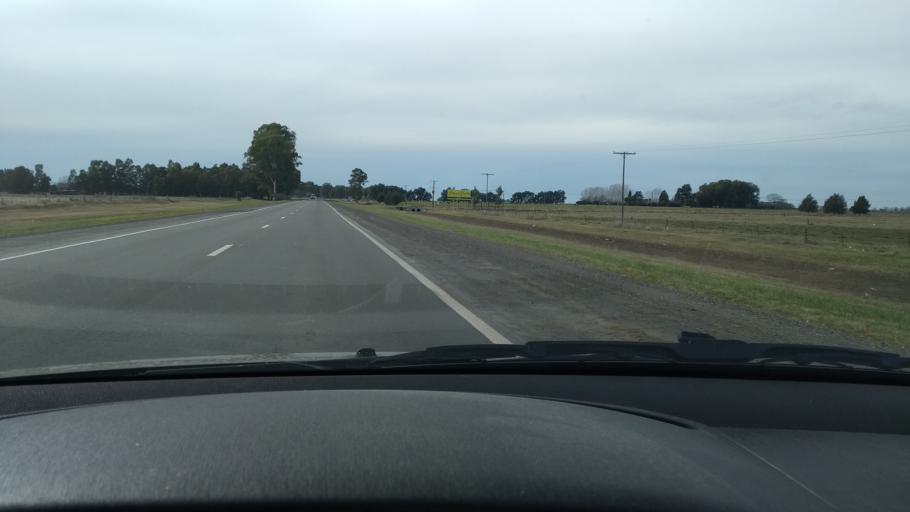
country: AR
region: Buenos Aires
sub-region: Partido de Azul
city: Azul
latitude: -36.7722
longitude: -59.8170
